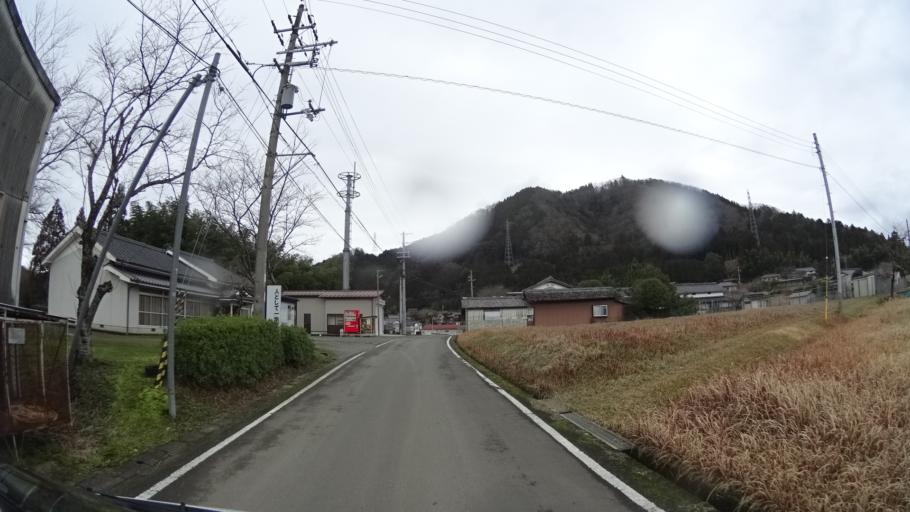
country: JP
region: Kyoto
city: Ayabe
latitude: 35.3260
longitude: 135.3551
